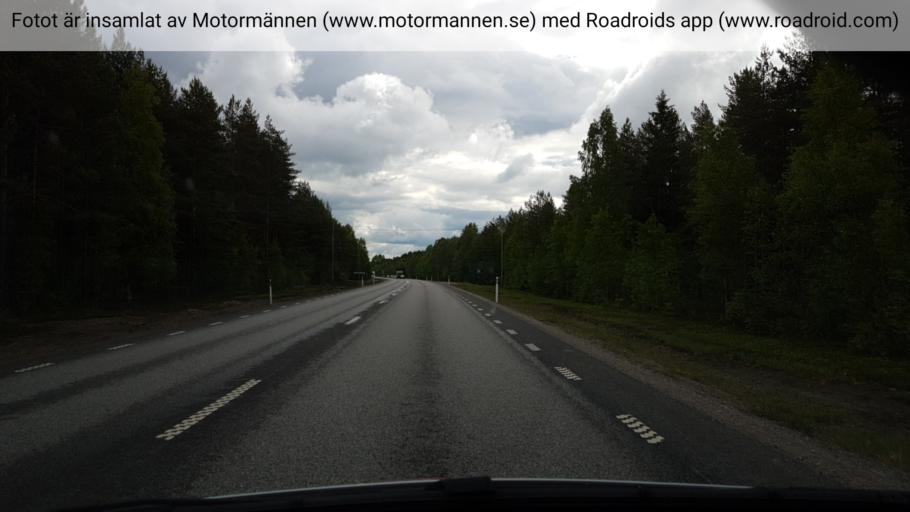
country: SE
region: Vaesterbotten
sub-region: Umea Kommun
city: Roback
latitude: 63.8501
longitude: 20.1178
